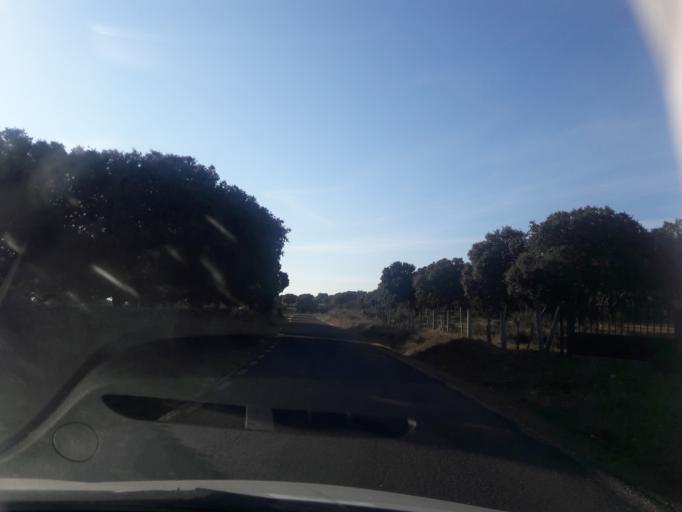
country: ES
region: Castille and Leon
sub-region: Provincia de Salamanca
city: Montejo
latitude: 40.6217
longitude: -5.6094
